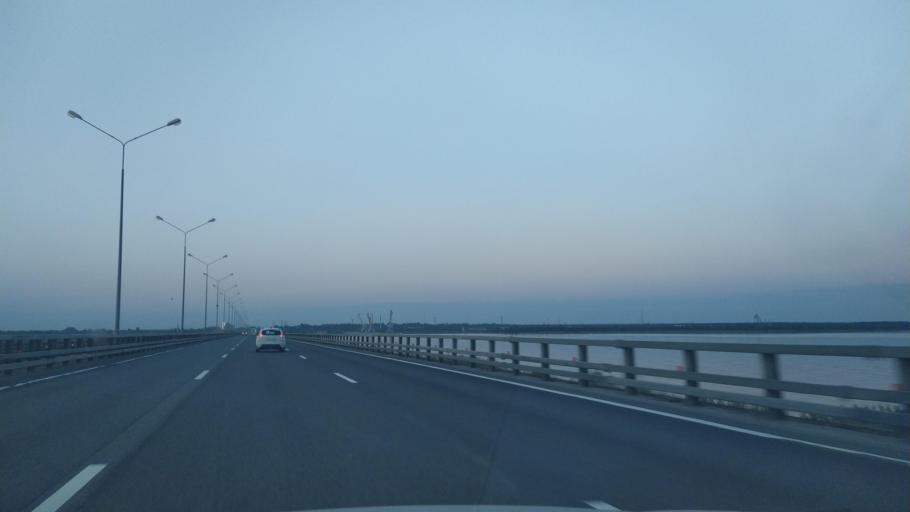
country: RU
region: Leningrad
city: Gorskaya
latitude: 60.0354
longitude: 29.9365
